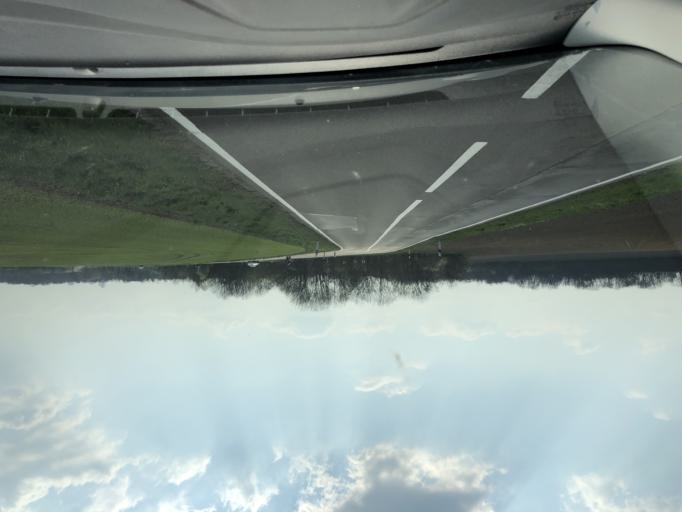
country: DE
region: Saxony-Anhalt
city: Niemberg
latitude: 51.5774
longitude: 12.0643
